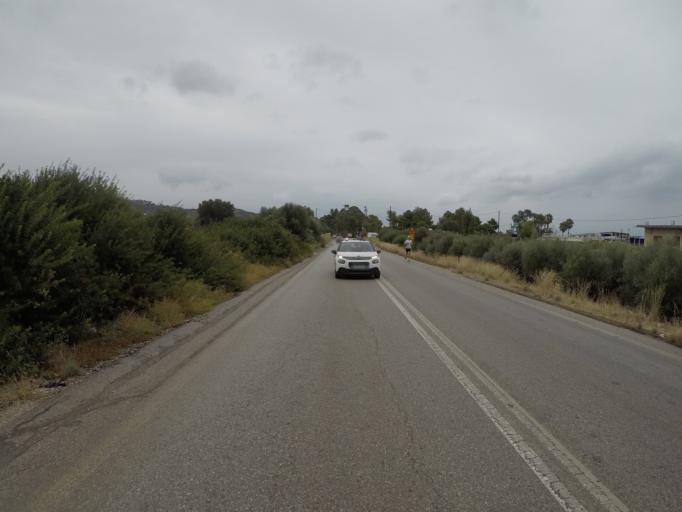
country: GR
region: Peloponnese
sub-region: Nomos Korinthias
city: Agioi Theodoroi
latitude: 37.9193
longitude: 23.0843
